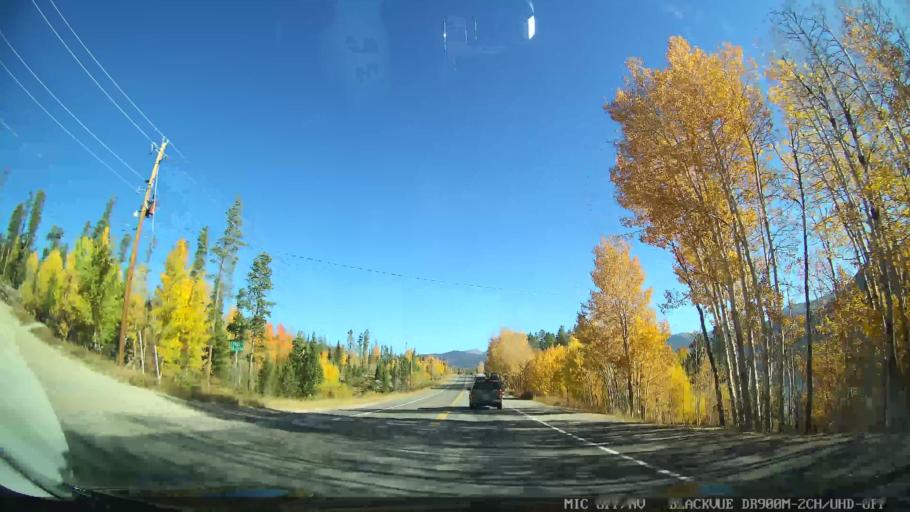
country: US
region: Colorado
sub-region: Grand County
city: Granby
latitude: 40.2290
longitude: -105.8506
